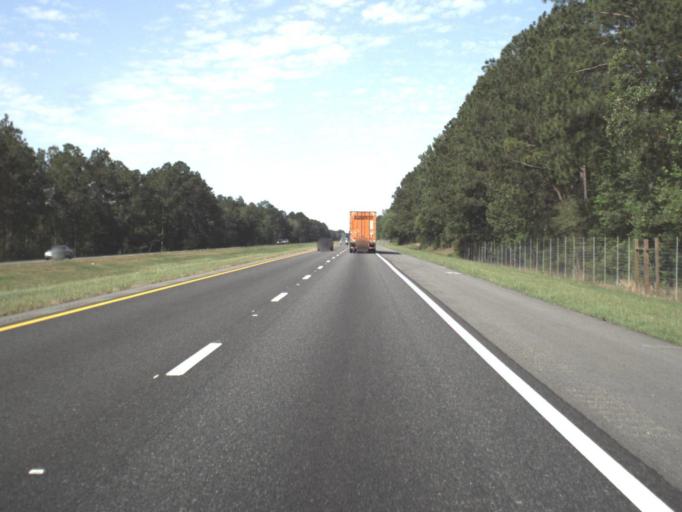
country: US
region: Florida
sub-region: Holmes County
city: Bonifay
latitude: 30.7427
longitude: -85.8753
